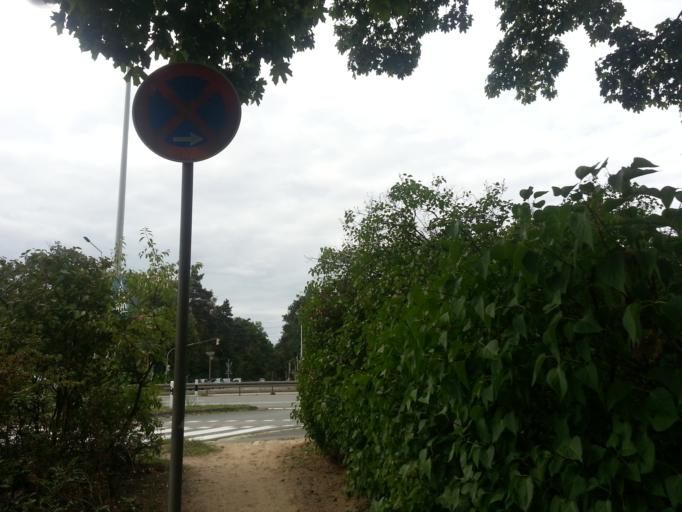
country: DE
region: Hesse
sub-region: Regierungsbezirk Darmstadt
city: Darmstadt
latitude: 49.8684
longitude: 8.6216
